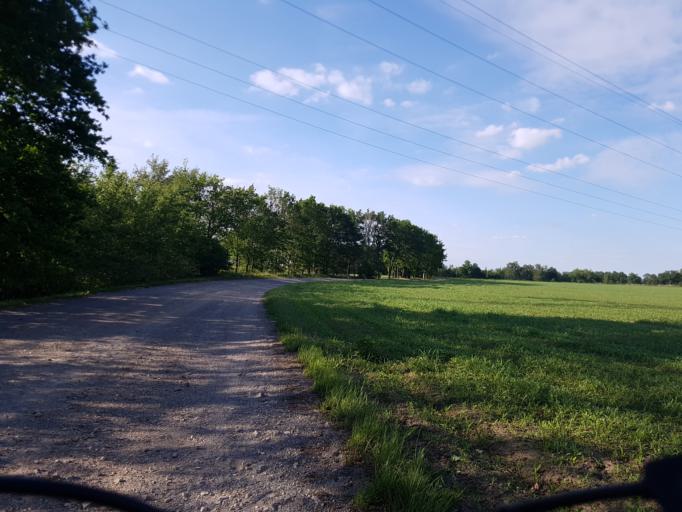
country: DE
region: Brandenburg
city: Merzdorf
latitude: 51.4266
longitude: 13.5268
